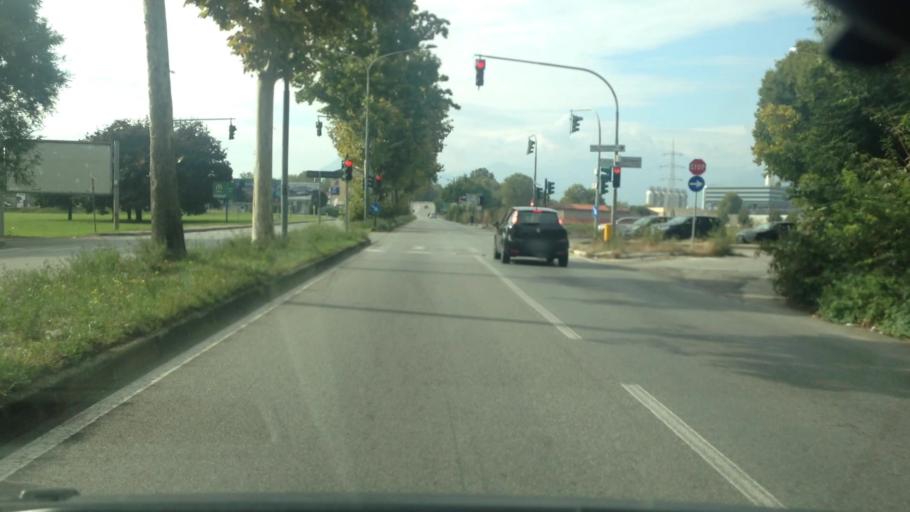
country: IT
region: Piedmont
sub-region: Provincia di Torino
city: Savonera
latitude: 45.0990
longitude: 7.6235
